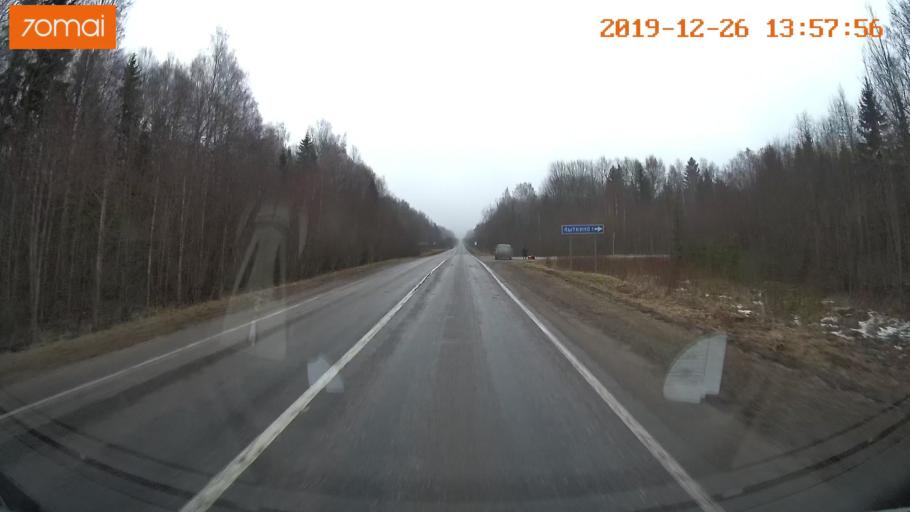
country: RU
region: Jaroslavl
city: Poshekhon'ye
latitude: 58.5782
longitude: 38.6900
